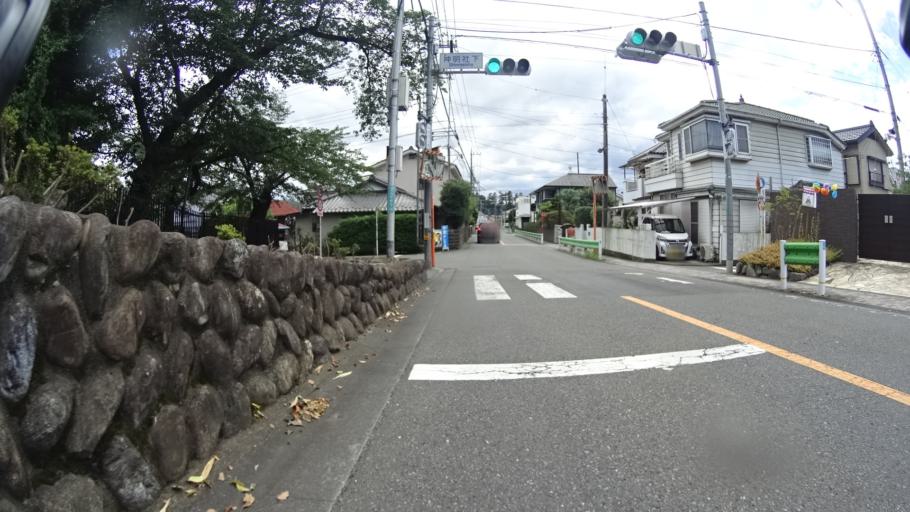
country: JP
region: Tokyo
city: Fussa
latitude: 35.7442
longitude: 139.3232
